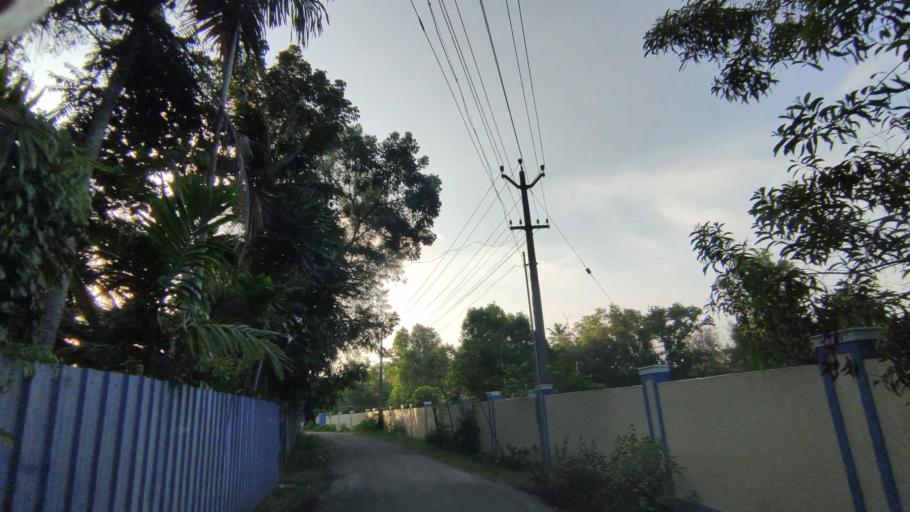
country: IN
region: Kerala
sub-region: Alappuzha
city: Shertallai
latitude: 9.6525
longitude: 76.3501
